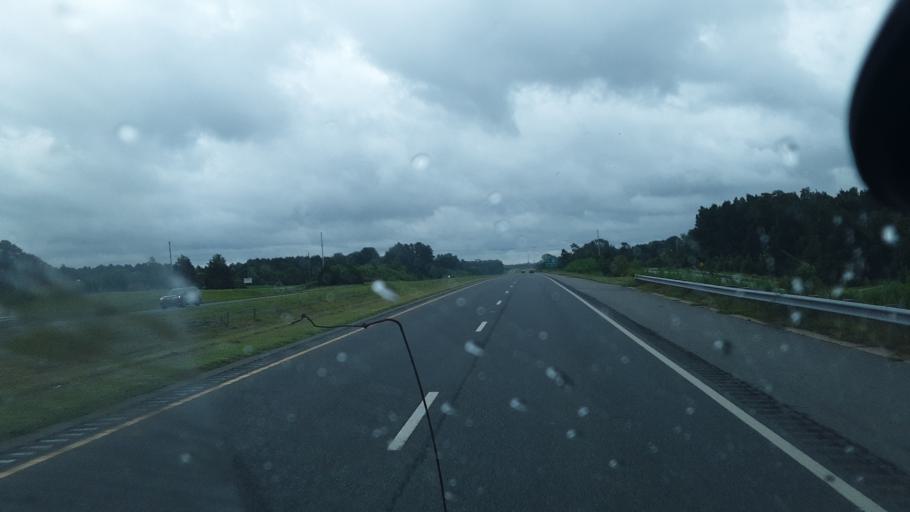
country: US
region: North Carolina
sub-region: Randolph County
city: Randleman
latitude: 35.8061
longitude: -79.8476
